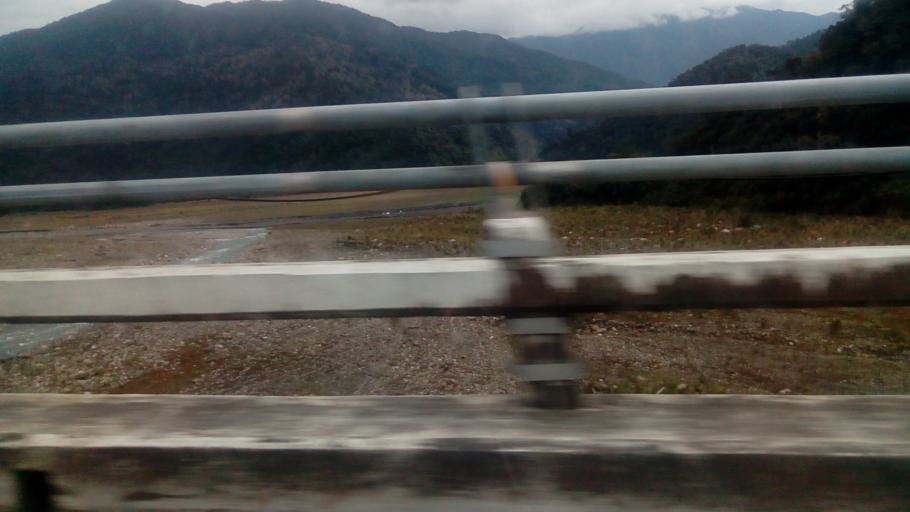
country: TW
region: Taiwan
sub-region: Yilan
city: Yilan
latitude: 24.5781
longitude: 121.4932
